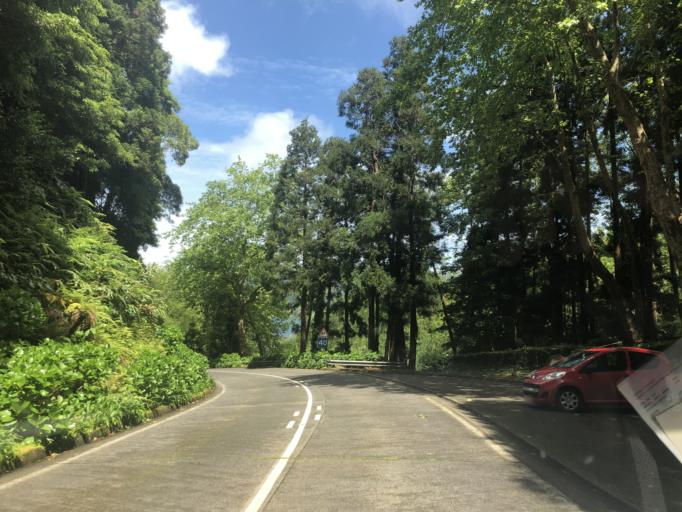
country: PT
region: Azores
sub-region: Ponta Delgada
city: Arrifes
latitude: 37.8511
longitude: -25.7825
